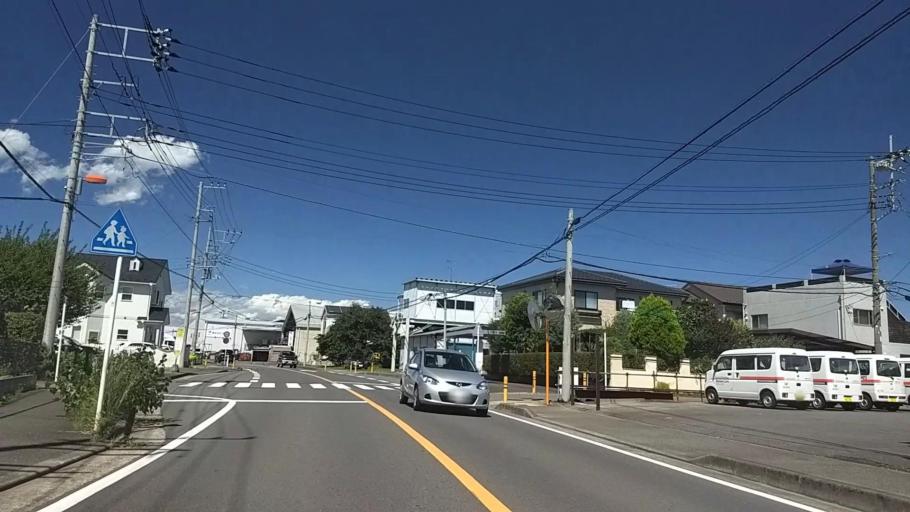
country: JP
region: Tokyo
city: Hachioji
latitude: 35.5631
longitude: 139.3262
